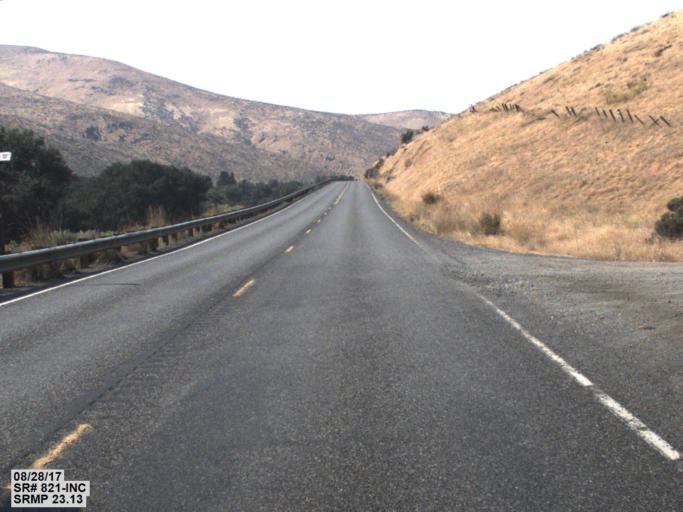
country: US
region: Washington
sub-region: Kittitas County
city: Ellensburg
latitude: 46.9064
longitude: -120.4985
